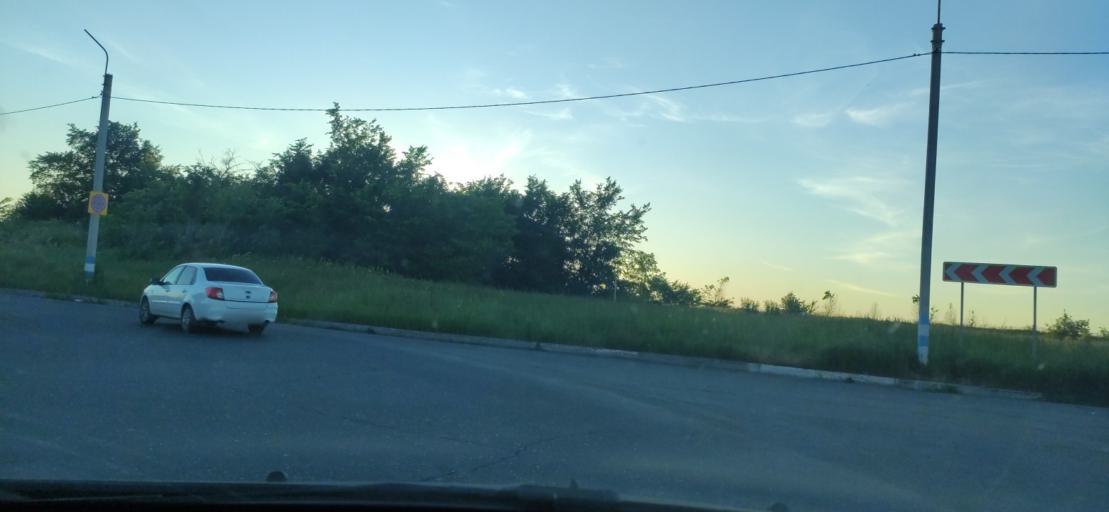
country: RU
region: Ulyanovsk
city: Mirnyy
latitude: 54.3789
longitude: 48.6716
